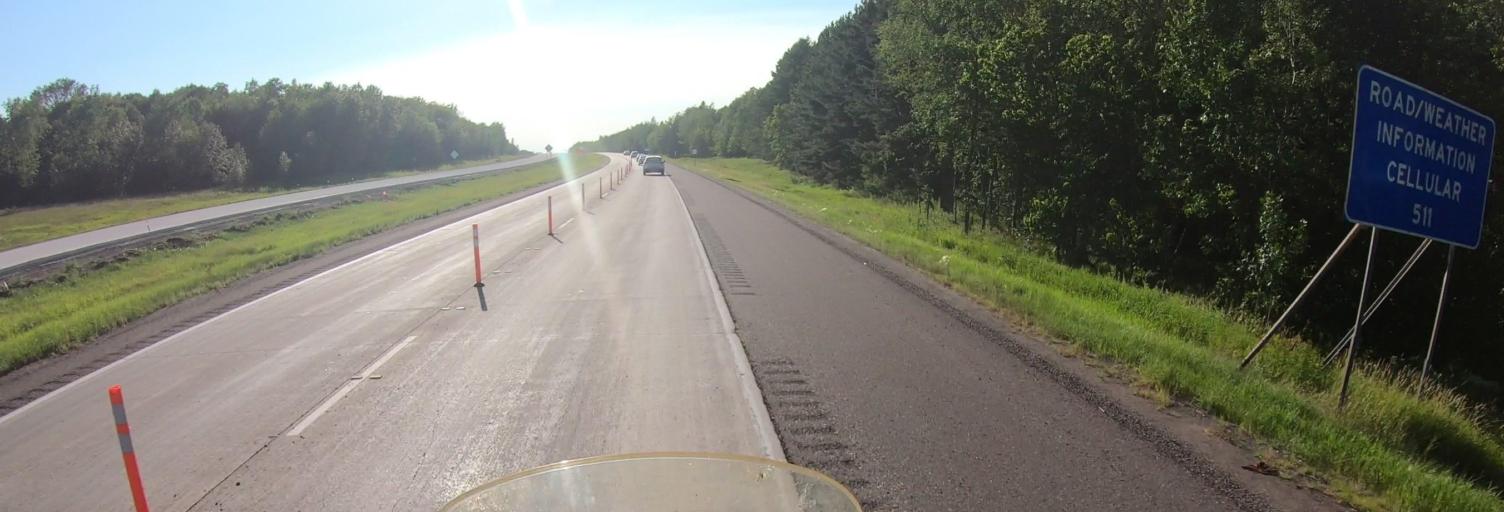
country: US
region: Minnesota
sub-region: Saint Louis County
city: Hermantown
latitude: 46.8520
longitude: -92.2902
